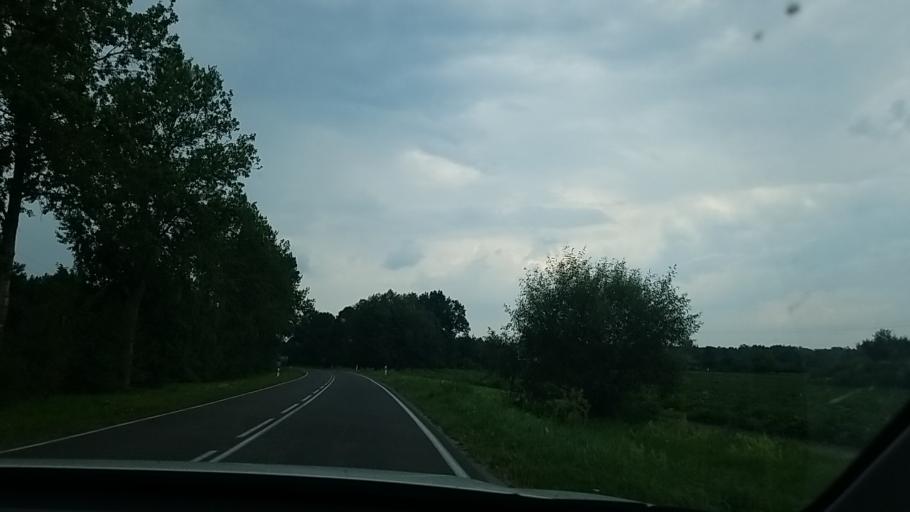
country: PL
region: Lublin Voivodeship
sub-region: Powiat leczynski
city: Cycow
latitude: 51.2427
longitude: 23.0895
